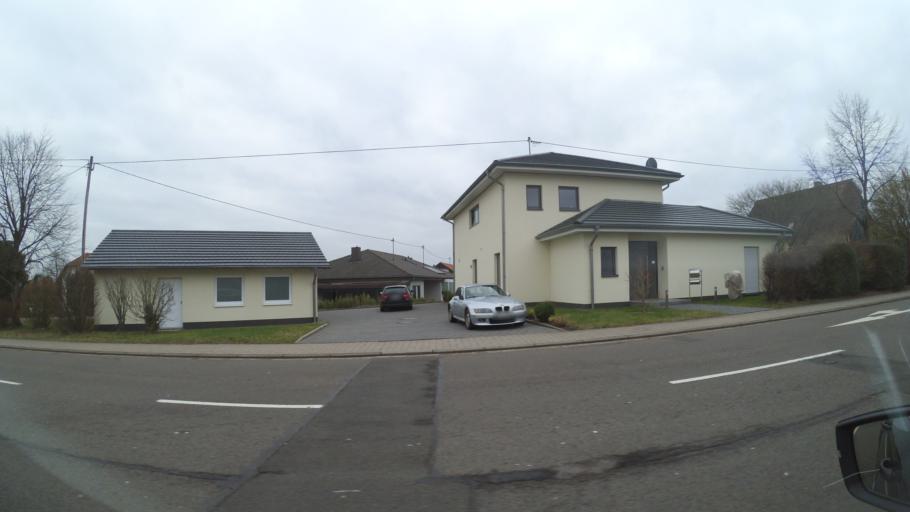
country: DE
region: Saarland
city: Illingen
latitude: 49.3727
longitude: 7.0171
